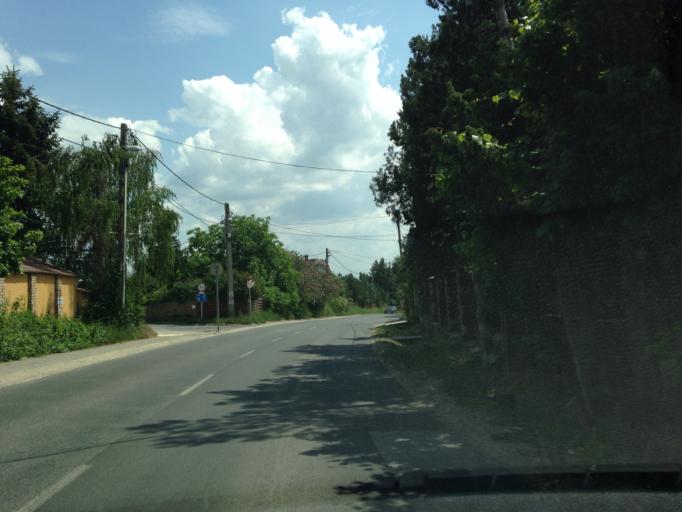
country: HU
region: Pest
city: Szentendre
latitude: 47.6830
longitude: 19.0618
